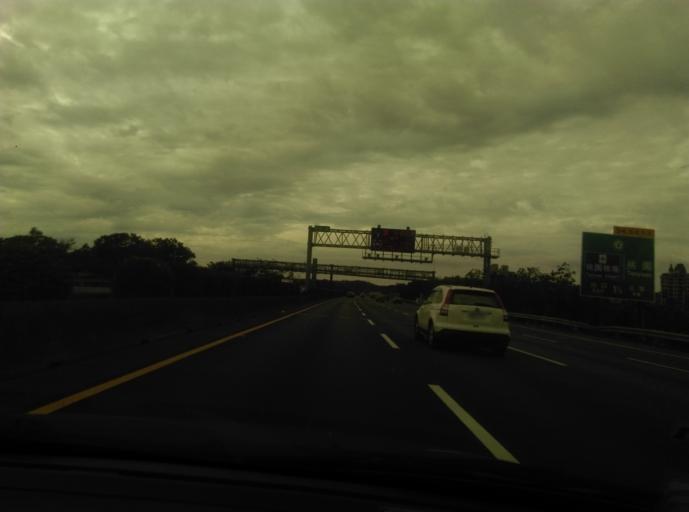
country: TW
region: Taiwan
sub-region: Taoyuan
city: Taoyuan
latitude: 24.9357
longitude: 121.3436
